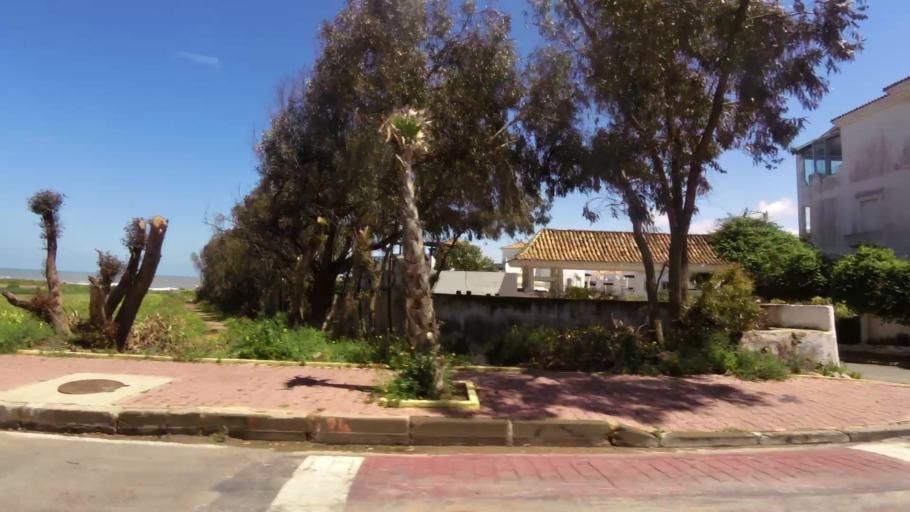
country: MA
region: Grand Casablanca
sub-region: Nouaceur
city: Dar Bouazza
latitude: 33.5296
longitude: -7.8207
